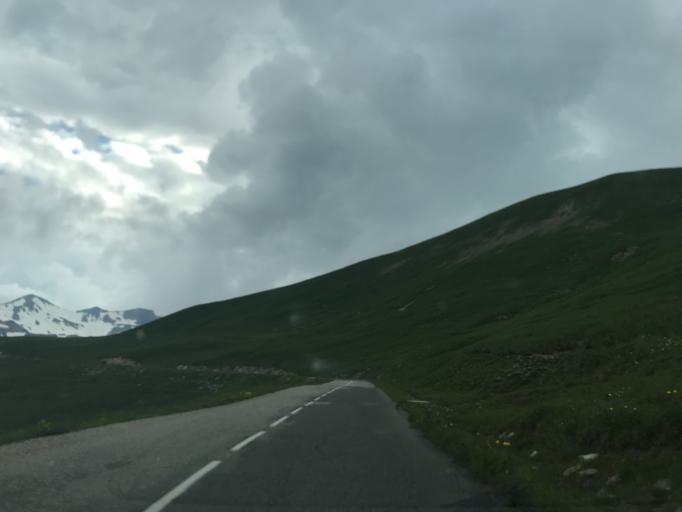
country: FR
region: Rhone-Alpes
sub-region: Departement de la Savoie
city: Valloire
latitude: 45.0809
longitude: 6.4194
